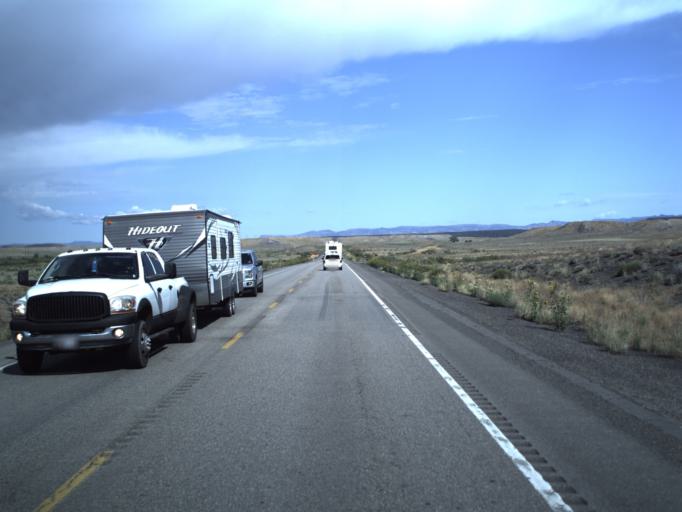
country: US
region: Utah
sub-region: Carbon County
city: East Carbon City
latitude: 39.4569
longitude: -110.4825
